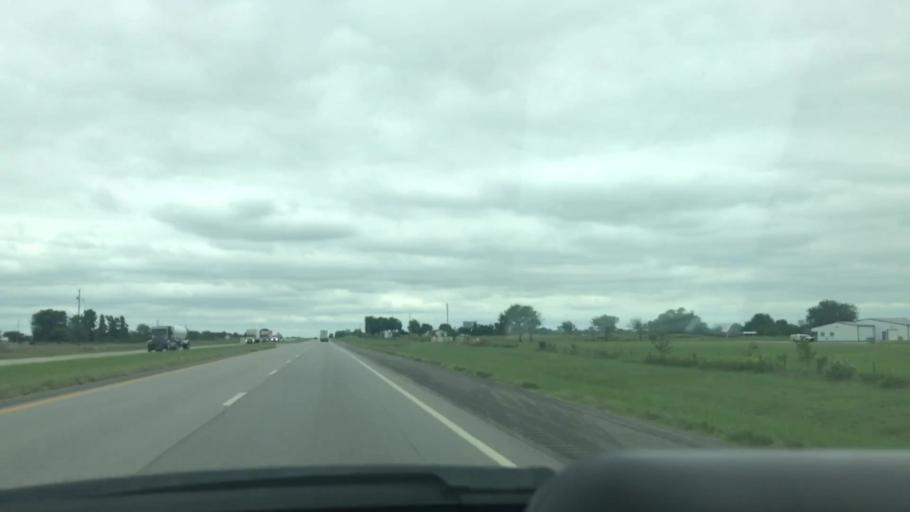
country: US
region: Oklahoma
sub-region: Mayes County
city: Pryor
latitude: 36.3241
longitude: -95.3126
